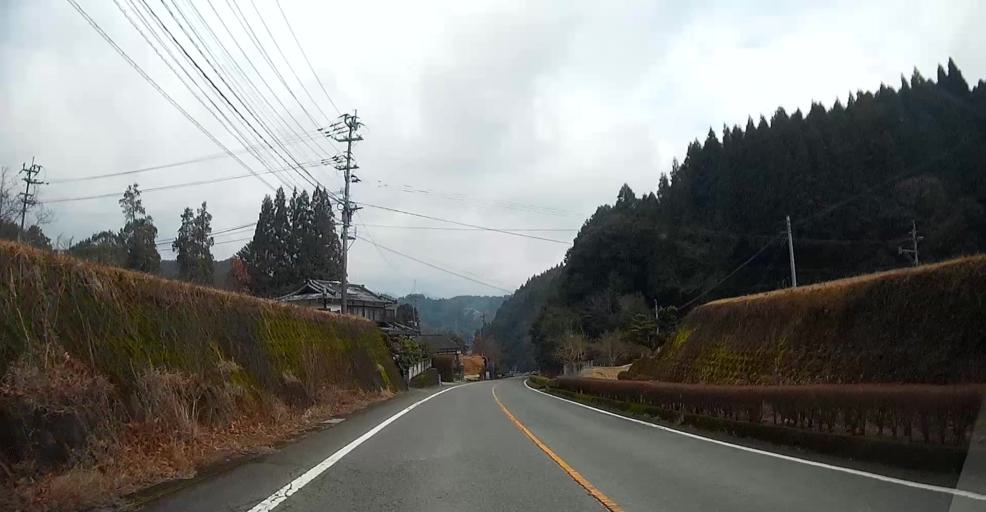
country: JP
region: Kumamoto
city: Matsubase
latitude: 32.6271
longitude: 130.8861
